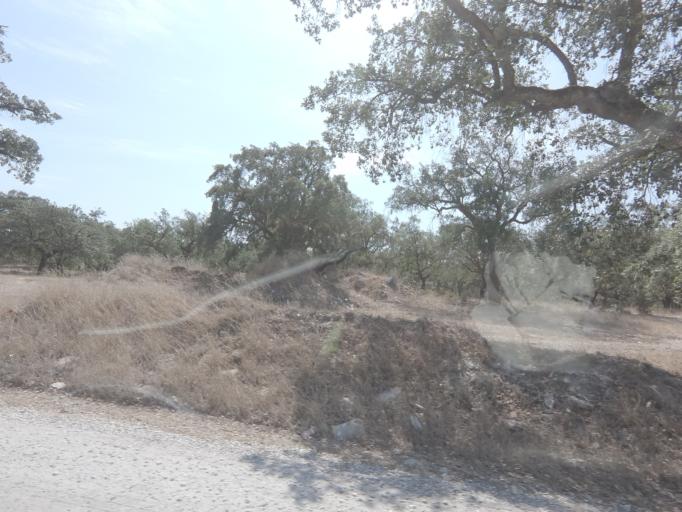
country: PT
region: Setubal
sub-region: Palmela
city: Palmela
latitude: 38.5897
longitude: -8.8520
